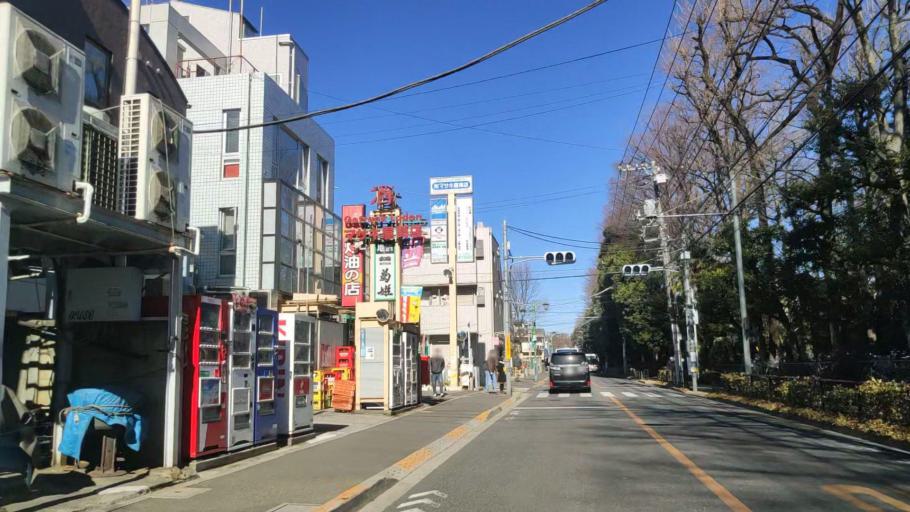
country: JP
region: Tokyo
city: Kamirenjaku
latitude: 35.6959
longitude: 139.5699
